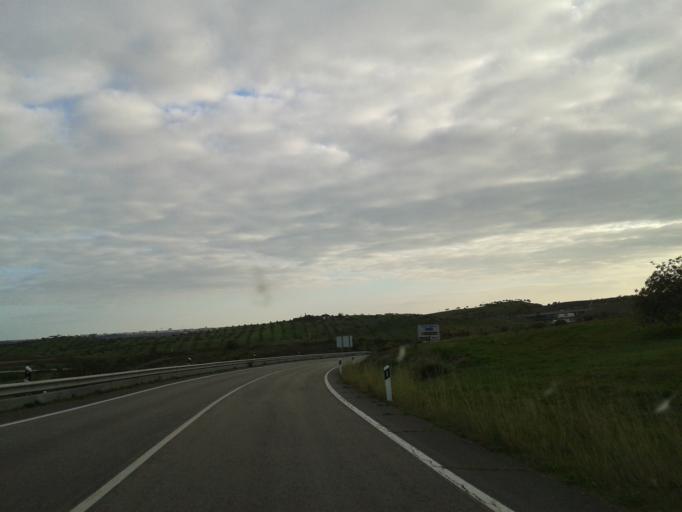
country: PT
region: Faro
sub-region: Castro Marim
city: Castro Marim
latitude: 37.2381
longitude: -7.4471
